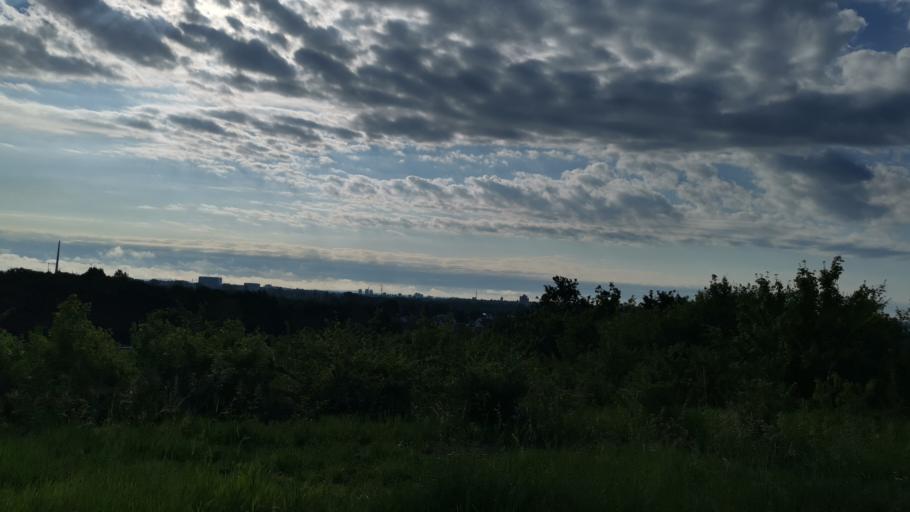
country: DE
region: Bavaria
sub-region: Regierungsbezirk Mittelfranken
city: Grossreuth bei Schweinau
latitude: 49.4209
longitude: 11.0492
